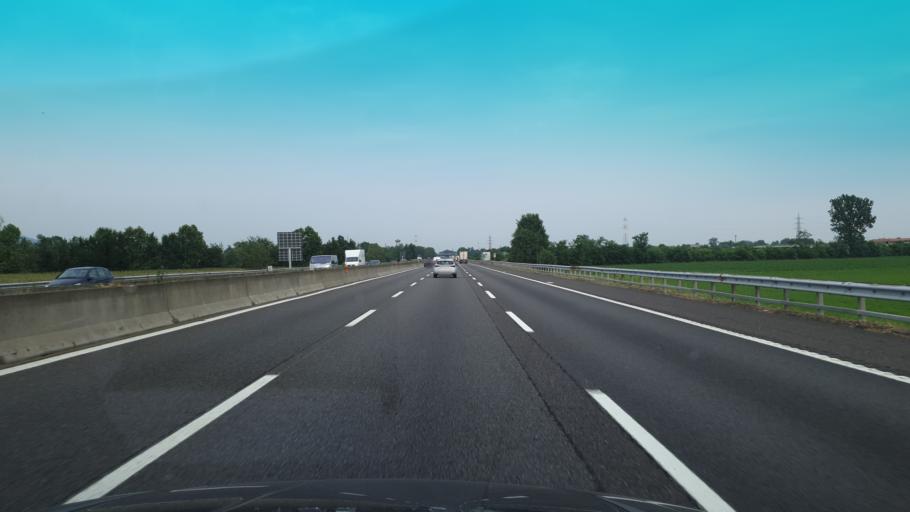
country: IT
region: Lombardy
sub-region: Provincia di Brescia
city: Roncadelle
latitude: 45.5404
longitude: 10.1332
